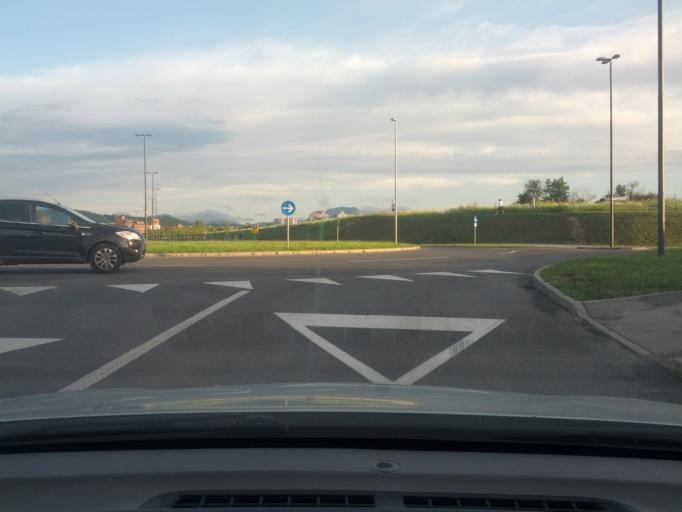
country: SI
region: Ljubljana
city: Ljubljana
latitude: 46.0756
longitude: 14.5246
